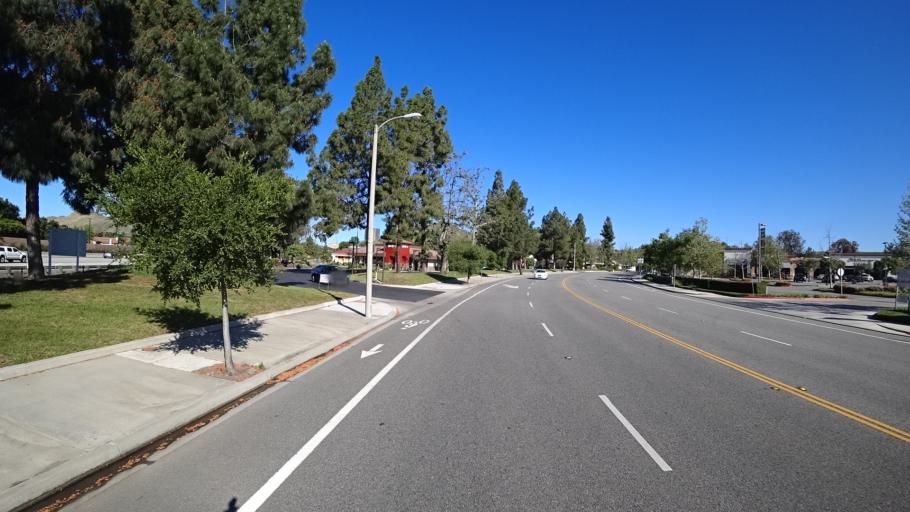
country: US
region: California
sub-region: Ventura County
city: Casa Conejo
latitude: 34.1885
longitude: -118.9348
